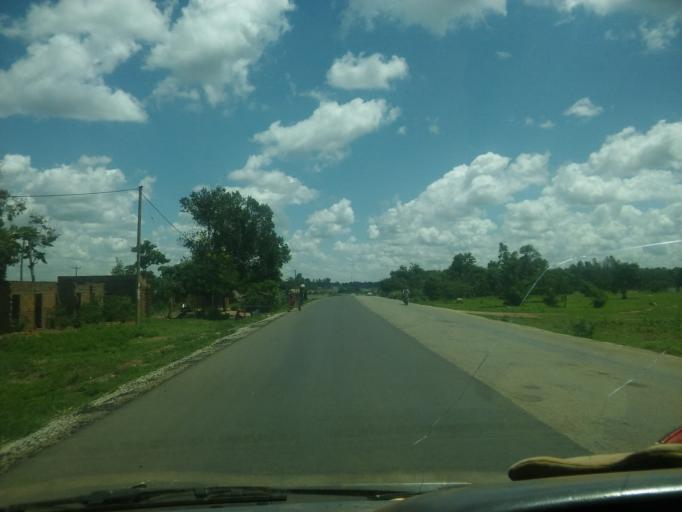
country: UG
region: Eastern Region
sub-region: Mbale District
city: Mbale
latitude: 1.0740
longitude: 34.1177
